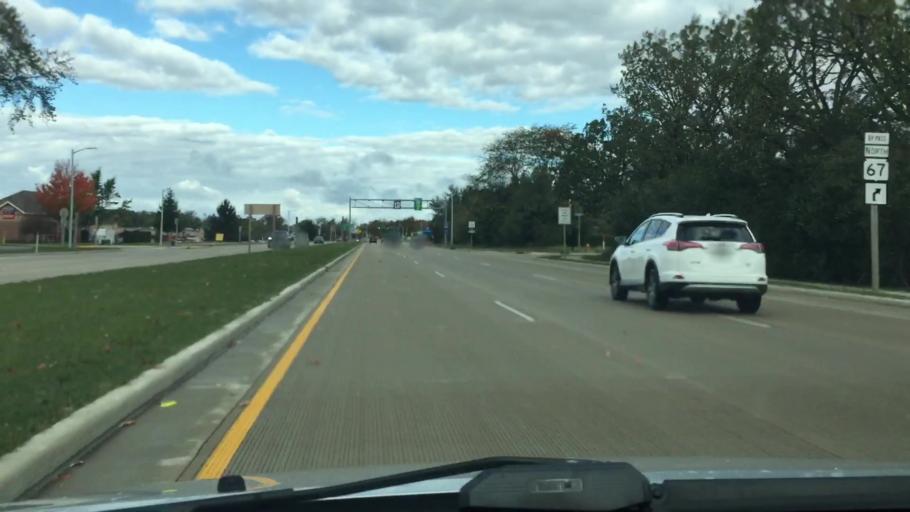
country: US
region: Wisconsin
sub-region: Waukesha County
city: Oconomowoc
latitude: 43.0931
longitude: -88.4780
